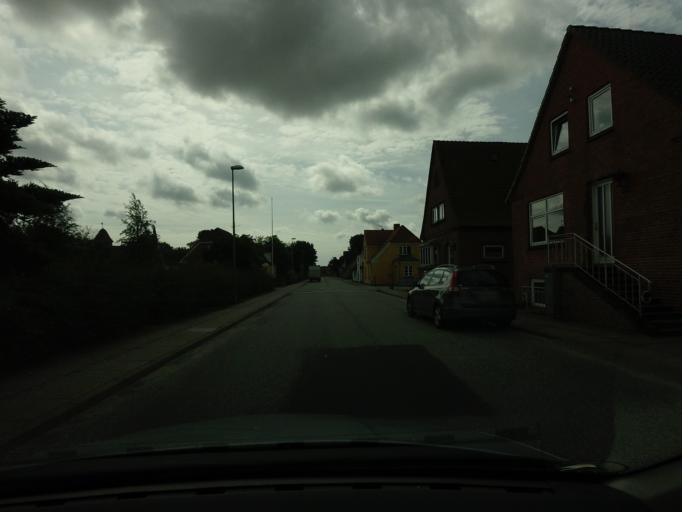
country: DK
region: North Denmark
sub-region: Bronderslev Kommune
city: Dronninglund
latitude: 57.2767
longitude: 10.3568
